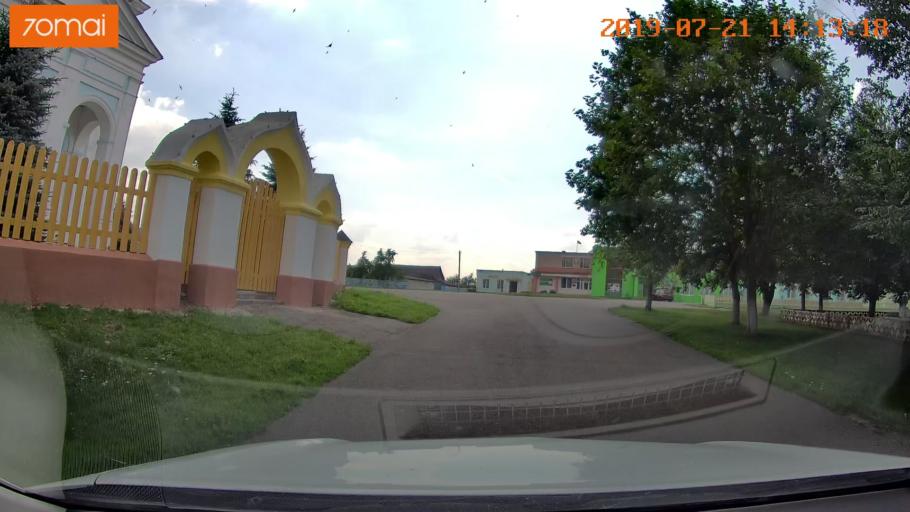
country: BY
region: Grodnenskaya
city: Karelichy
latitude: 53.6506
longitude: 26.1744
